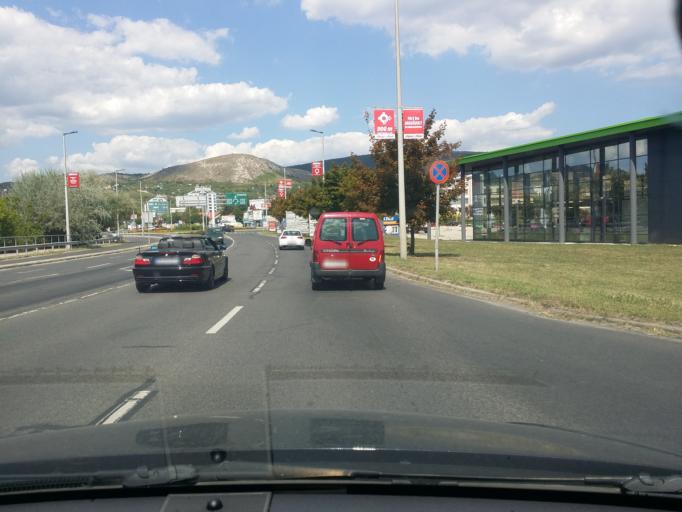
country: HU
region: Pest
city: Budaors
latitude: 47.4539
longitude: 18.9490
